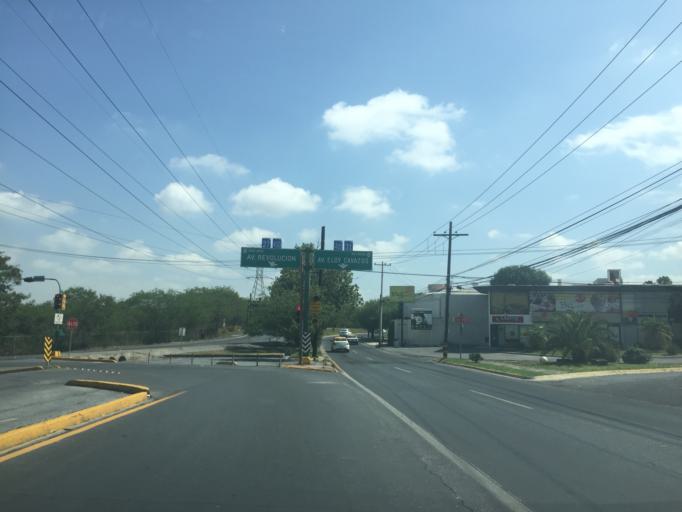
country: MX
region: Nuevo Leon
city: Guadalupe
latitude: 25.6474
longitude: -100.2677
